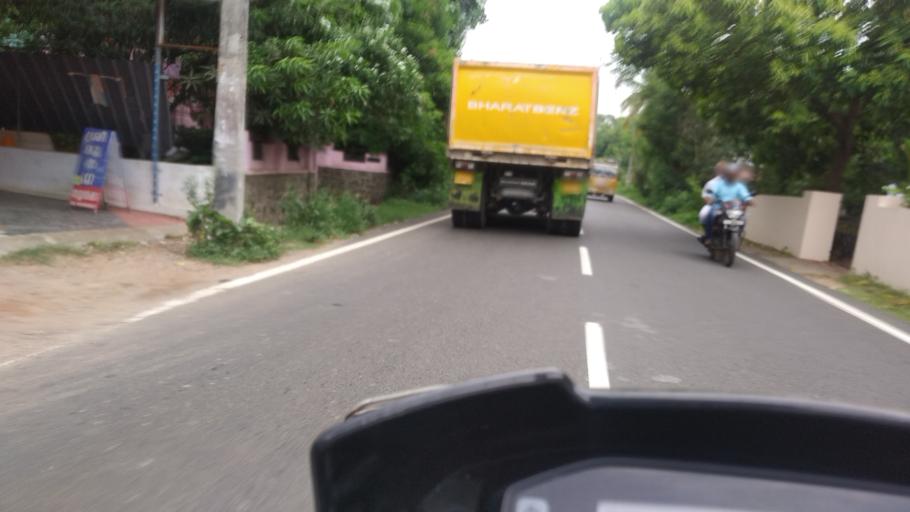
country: IN
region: Kerala
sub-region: Ernakulam
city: Aluva
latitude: 10.1550
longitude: 76.2803
